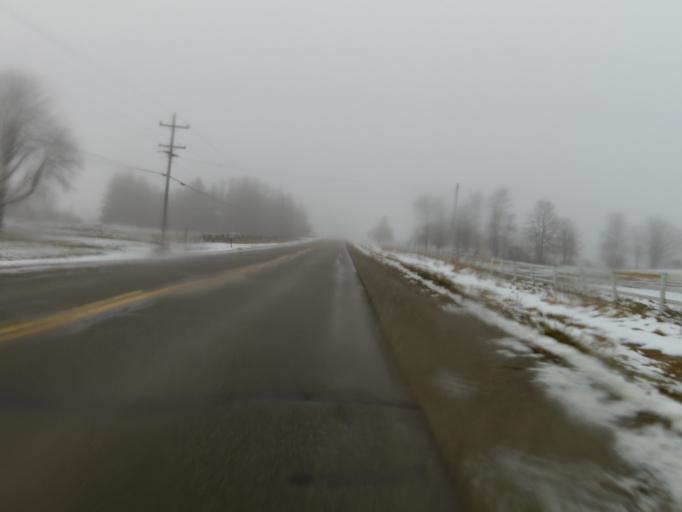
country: CA
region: Ontario
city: Perth
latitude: 44.8652
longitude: -76.3345
